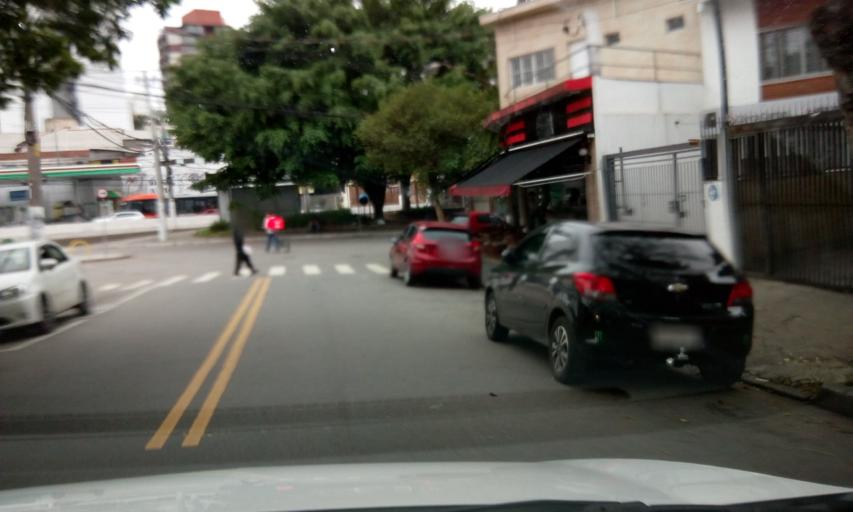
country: BR
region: Sao Paulo
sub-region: Sao Paulo
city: Sao Paulo
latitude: -23.5477
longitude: -46.6903
